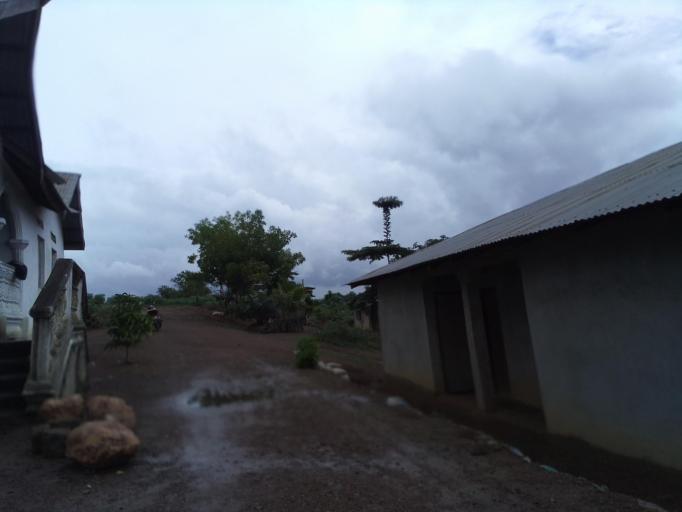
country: SL
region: Eastern Province
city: Kenema
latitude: 7.8812
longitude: -11.1627
